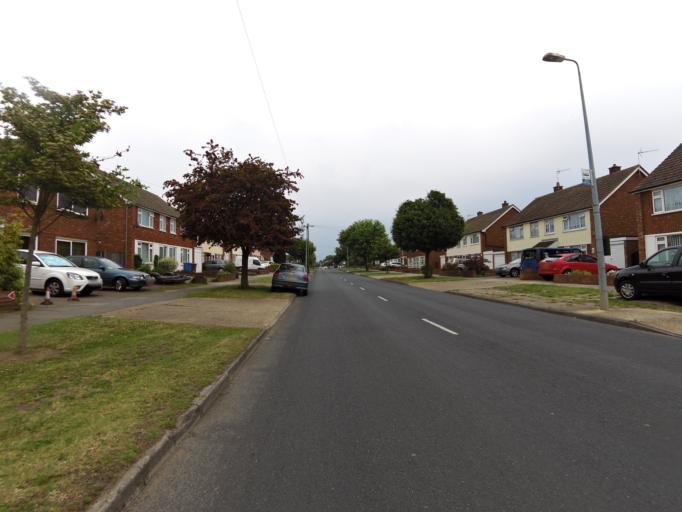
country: GB
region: England
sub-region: Suffolk
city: Ipswich
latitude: 52.0847
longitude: 1.1425
